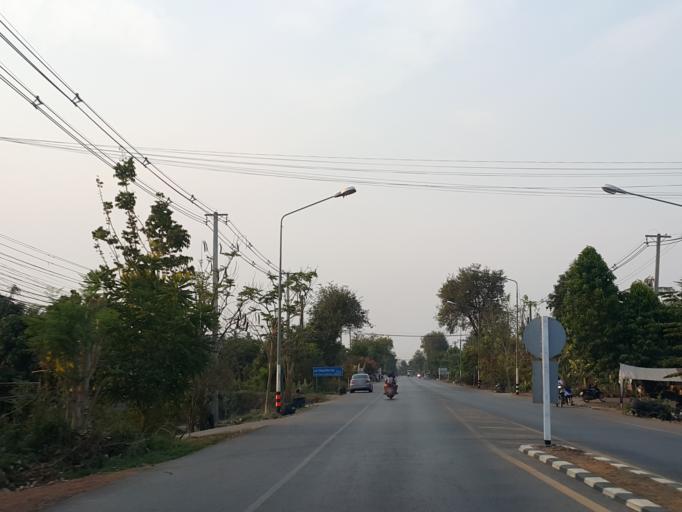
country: TH
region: Sukhothai
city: Sawankhalok
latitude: 17.2795
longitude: 99.8441
